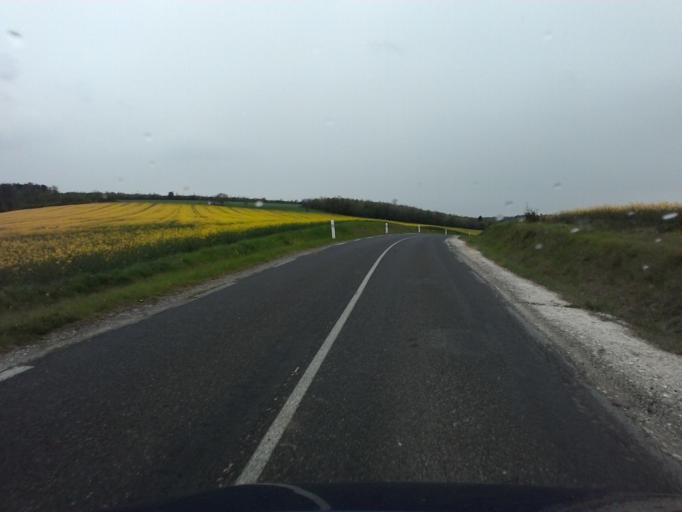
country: FR
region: Lorraine
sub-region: Departement de la Meuse
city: Gondrecourt-le-Chateau
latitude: 48.5636
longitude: 5.5340
